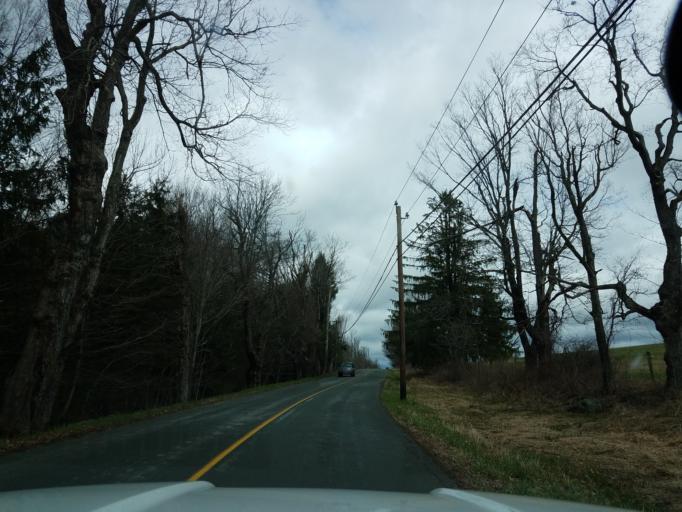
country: US
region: Connecticut
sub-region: Litchfield County
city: Litchfield
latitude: 41.7861
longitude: -73.1787
